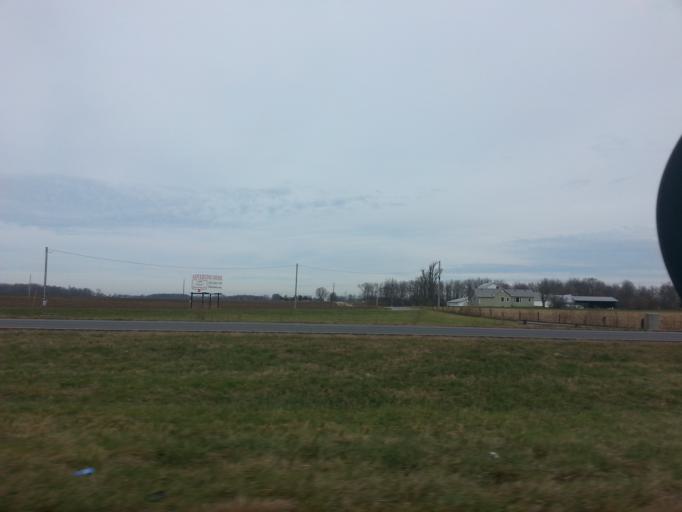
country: US
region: Indiana
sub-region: Hendricks County
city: Pittsboro
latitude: 39.8797
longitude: -86.4591
